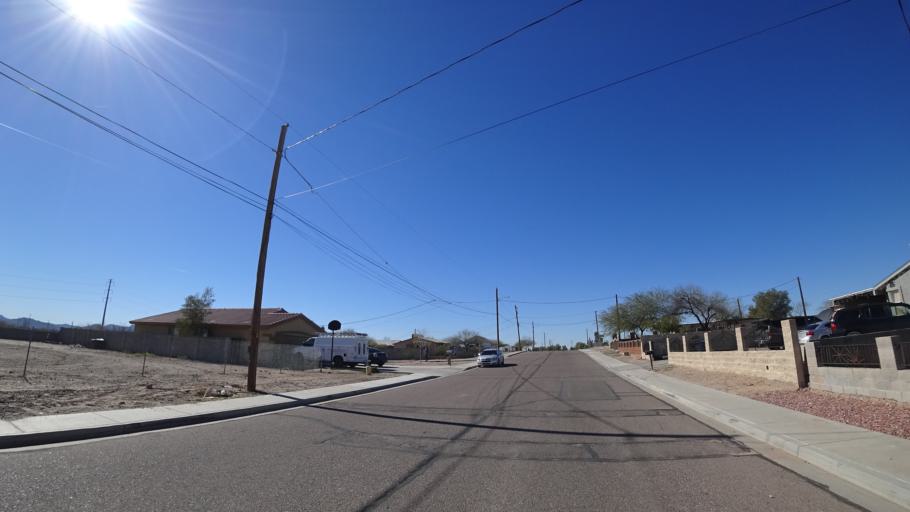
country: US
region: Arizona
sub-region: Maricopa County
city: Avondale
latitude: 33.4134
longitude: -112.3328
